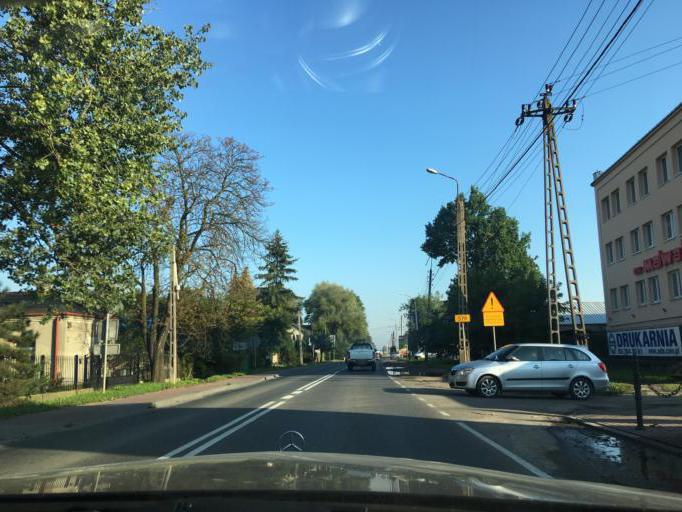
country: PL
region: Masovian Voivodeship
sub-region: Powiat grodziski
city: Grodzisk Mazowiecki
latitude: 52.1162
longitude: 20.6206
